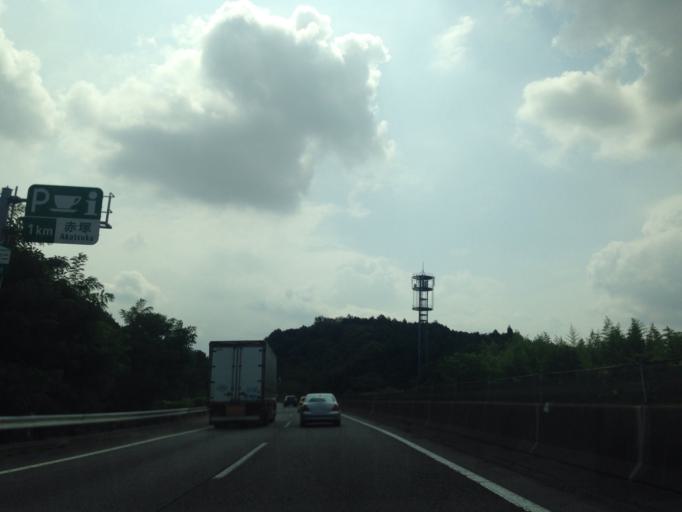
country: JP
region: Aichi
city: Kozakai-cho
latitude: 34.8498
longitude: 137.3498
